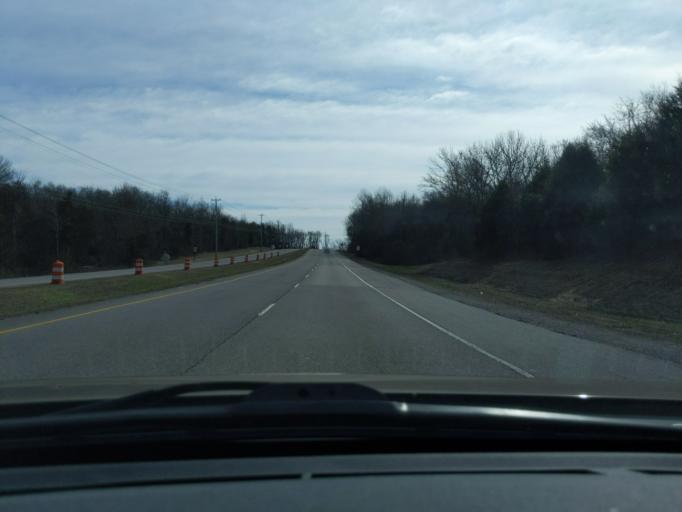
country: US
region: Tennessee
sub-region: Wilson County
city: Mount Juliet
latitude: 36.1843
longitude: -86.4611
